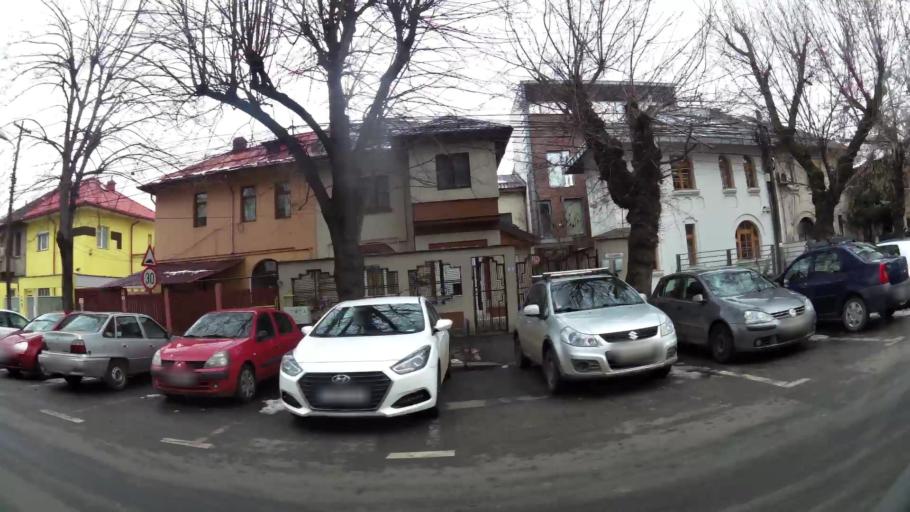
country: RO
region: Bucuresti
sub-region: Municipiul Bucuresti
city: Bucuresti
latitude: 44.4603
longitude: 26.0778
